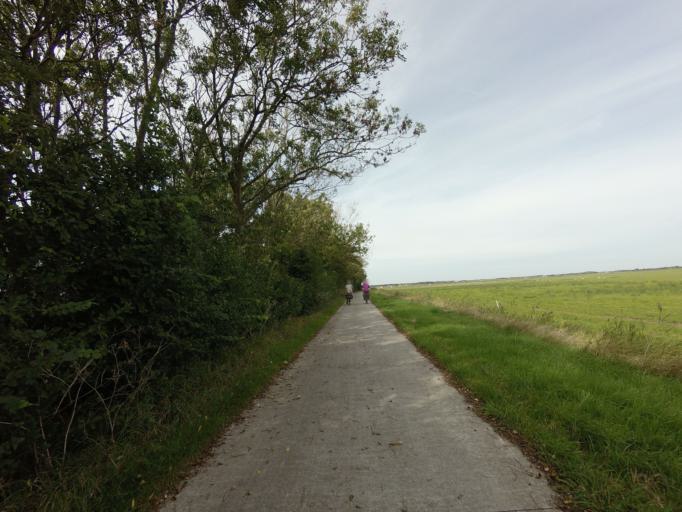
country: NL
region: North Holland
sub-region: Gemeente Texel
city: Den Burg
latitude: 53.0734
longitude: 4.8083
